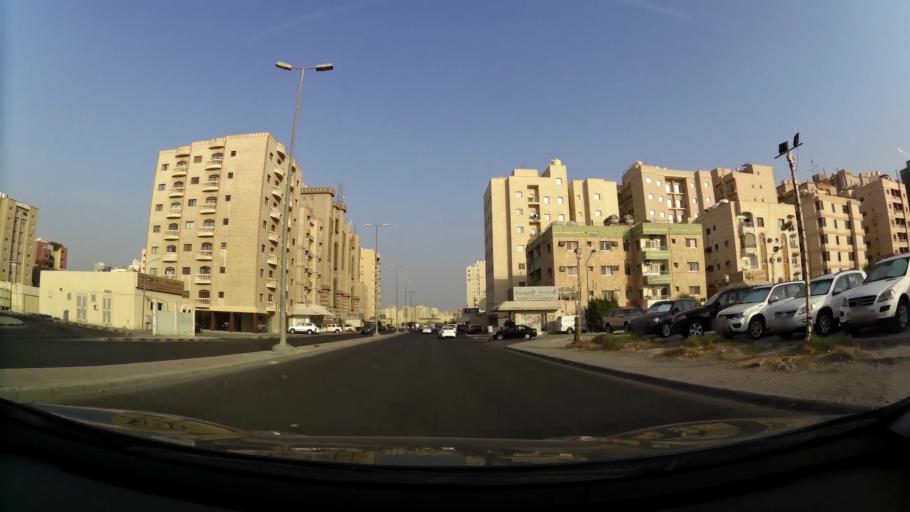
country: KW
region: Muhafazat Hawalli
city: As Salimiyah
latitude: 29.3324
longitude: 48.0650
